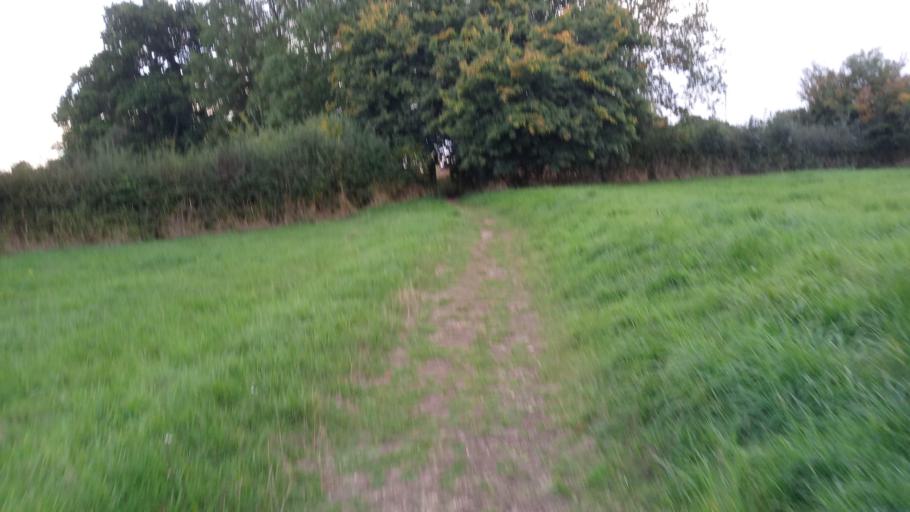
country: GB
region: England
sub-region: Cambridgeshire
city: Linton
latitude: 52.0547
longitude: 0.3063
